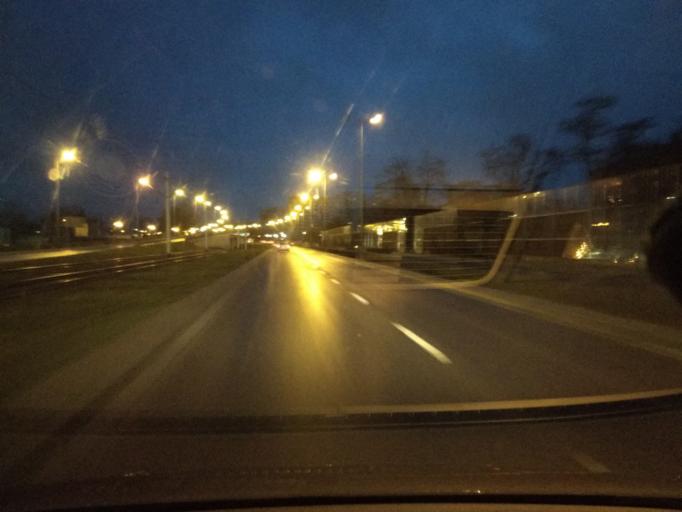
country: PL
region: Lower Silesian Voivodeship
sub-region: Powiat wroclawski
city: Wroclaw
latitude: 51.1339
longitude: 16.9553
